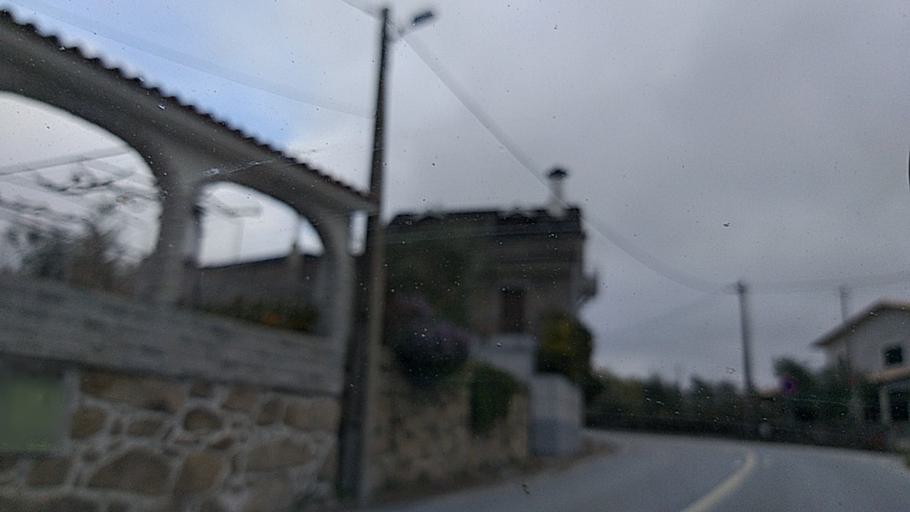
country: PT
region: Guarda
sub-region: Fornos de Algodres
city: Fornos de Algodres
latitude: 40.6545
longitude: -7.4852
